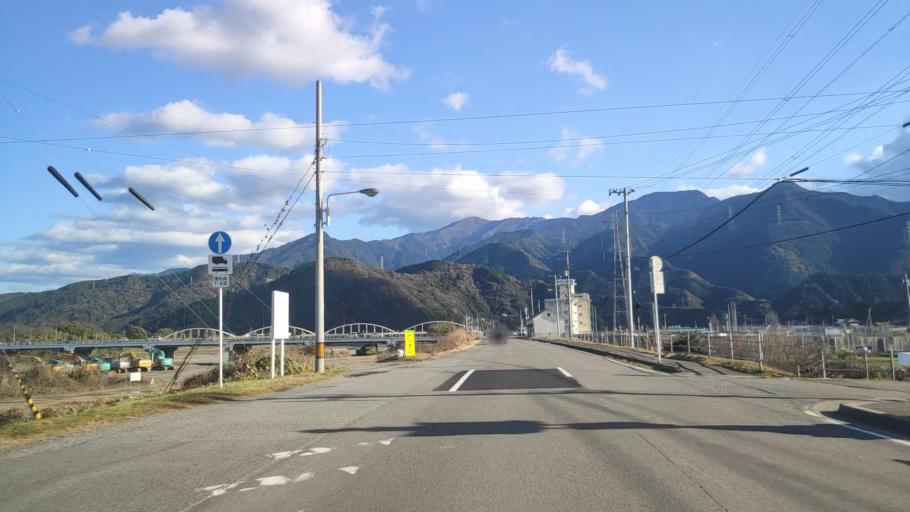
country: JP
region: Ehime
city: Saijo
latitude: 33.9035
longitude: 133.1814
